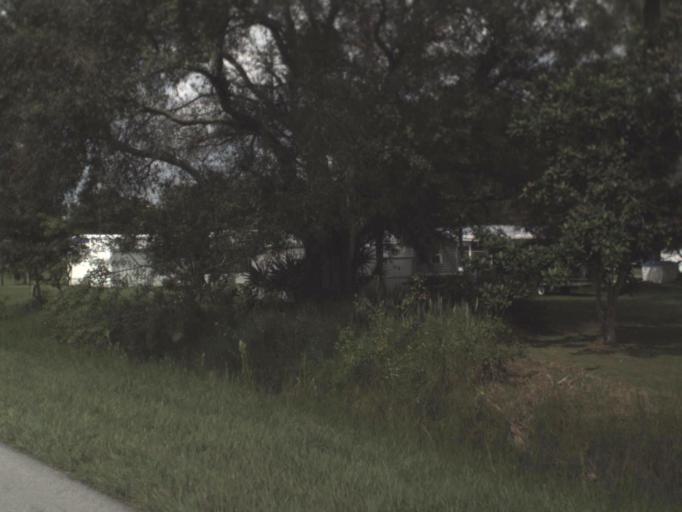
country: US
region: Florida
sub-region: Glades County
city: Buckhead Ridge
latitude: 27.2363
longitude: -81.0049
